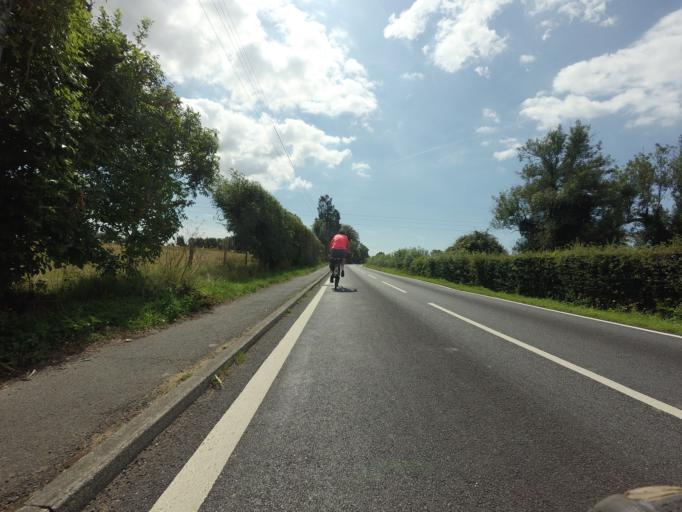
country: GB
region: England
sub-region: Kent
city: Stone
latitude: 51.0379
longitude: 0.7863
